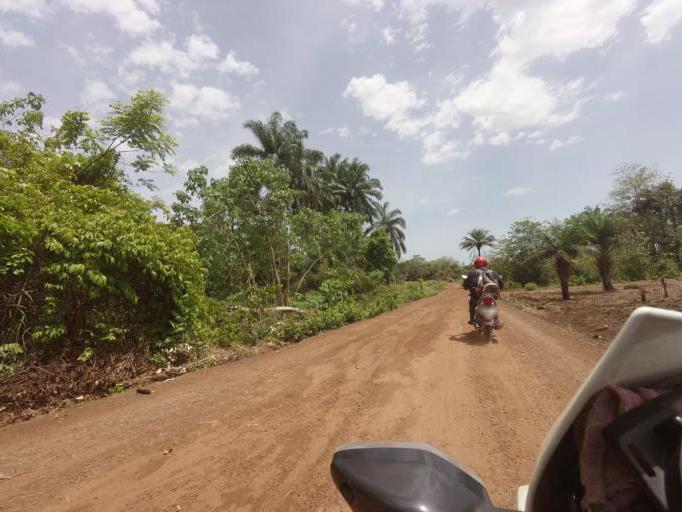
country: SL
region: Northern Province
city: Kamakwie
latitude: 9.5147
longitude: -12.2705
